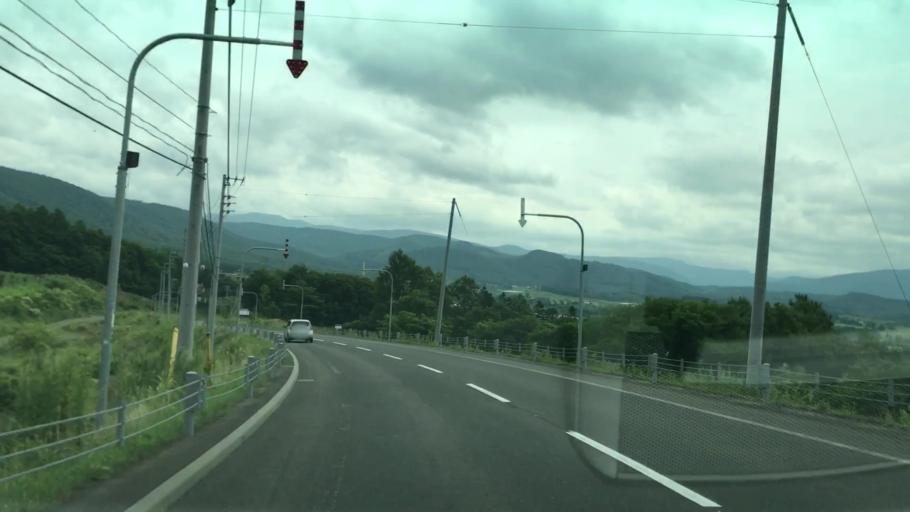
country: JP
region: Hokkaido
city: Yoichi
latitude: 43.1093
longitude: 140.8200
